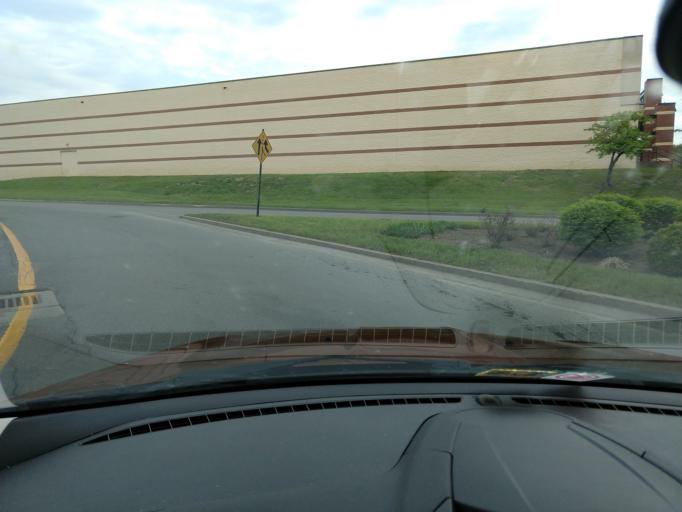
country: US
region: West Virginia
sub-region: Harrison County
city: Bridgeport
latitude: 39.3149
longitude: -80.2738
